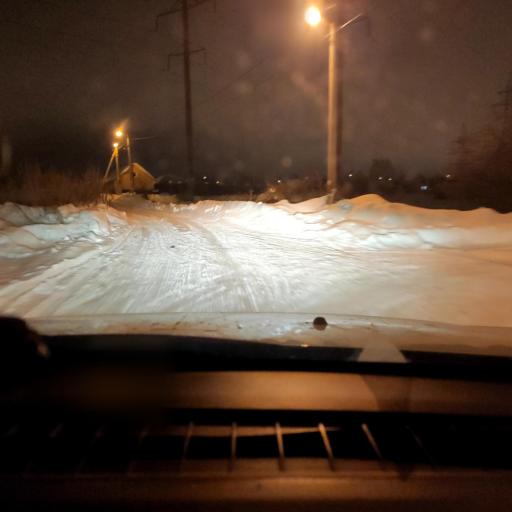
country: RU
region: Samara
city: Petra-Dubrava
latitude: 53.2904
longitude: 50.3121
